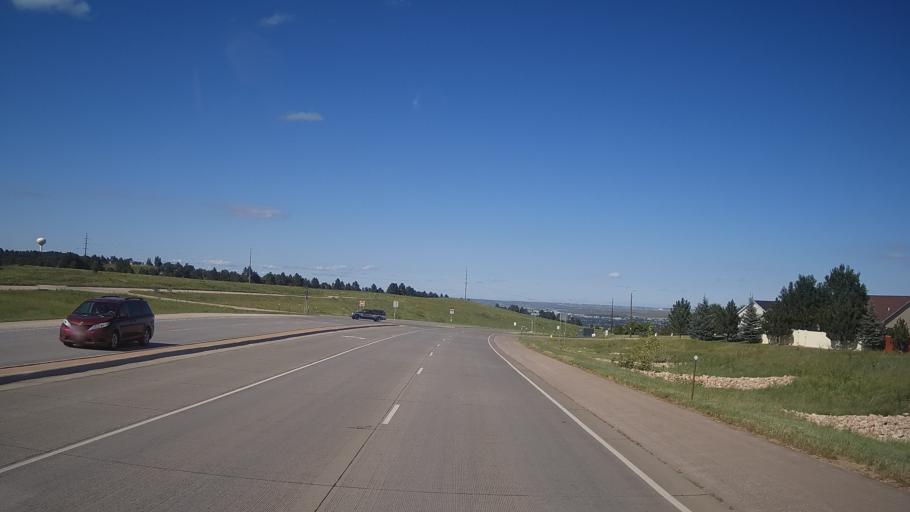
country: US
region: South Dakota
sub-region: Pennington County
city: Rapid City
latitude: 44.0198
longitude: -103.2426
